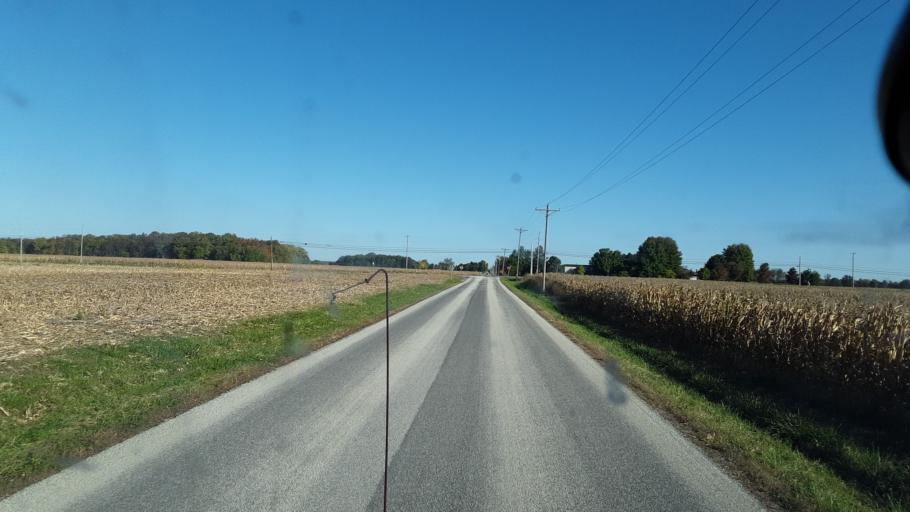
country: US
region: Ohio
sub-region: Hardin County
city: Kenton
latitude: 40.6421
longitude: -83.5380
